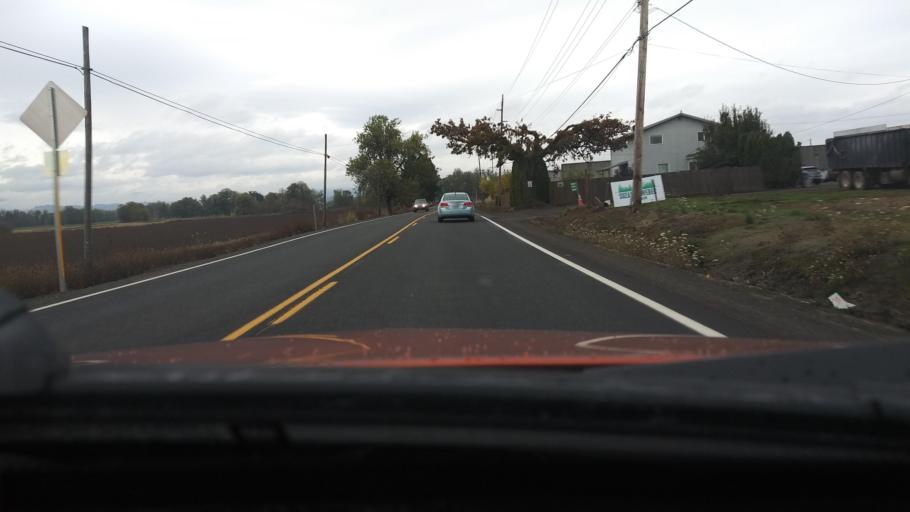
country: US
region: Oregon
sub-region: Washington County
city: Forest Grove
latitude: 45.5669
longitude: -123.1067
